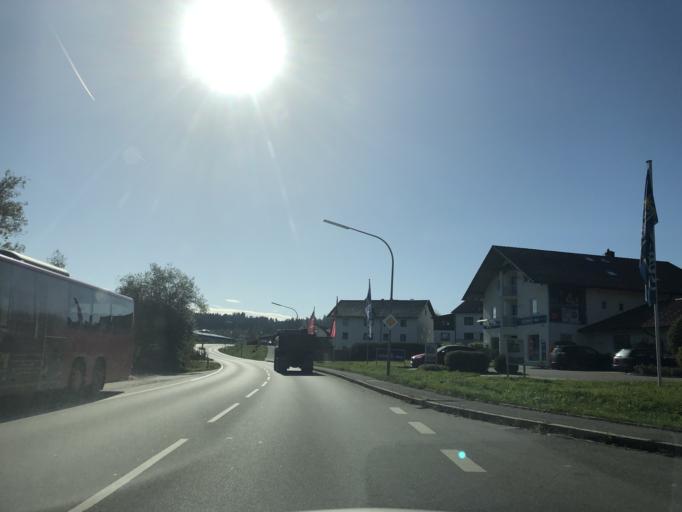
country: DE
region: Bavaria
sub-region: Lower Bavaria
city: Teisnach
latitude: 49.0322
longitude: 12.9916
